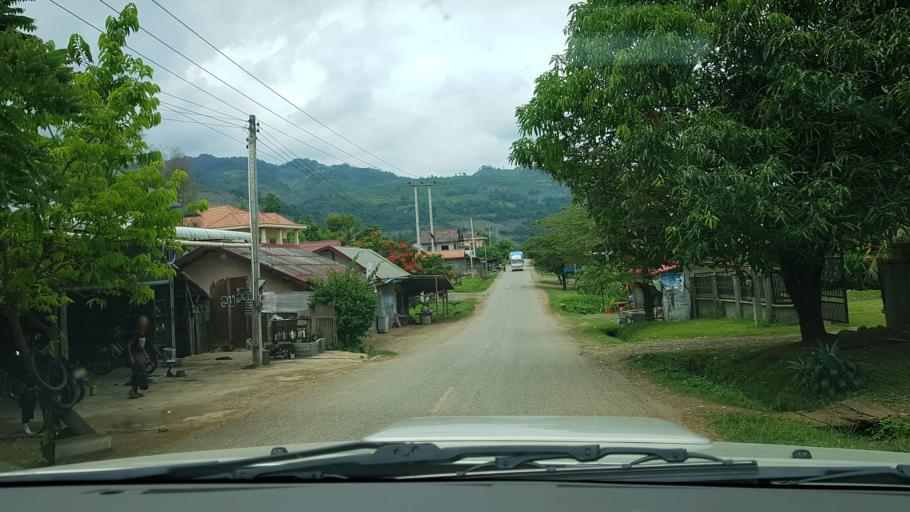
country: TH
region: Nan
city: Chaloem Phra Kiat
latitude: 19.9883
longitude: 101.2770
